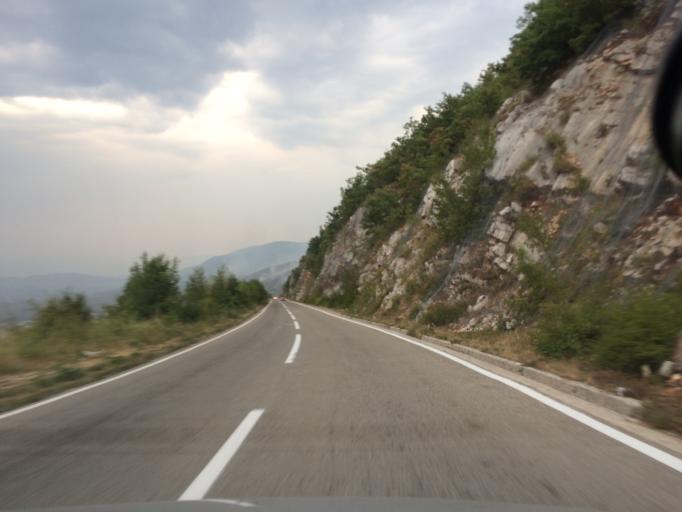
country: ME
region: Opstina Niksic
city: Niksic
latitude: 42.8856
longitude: 18.9517
